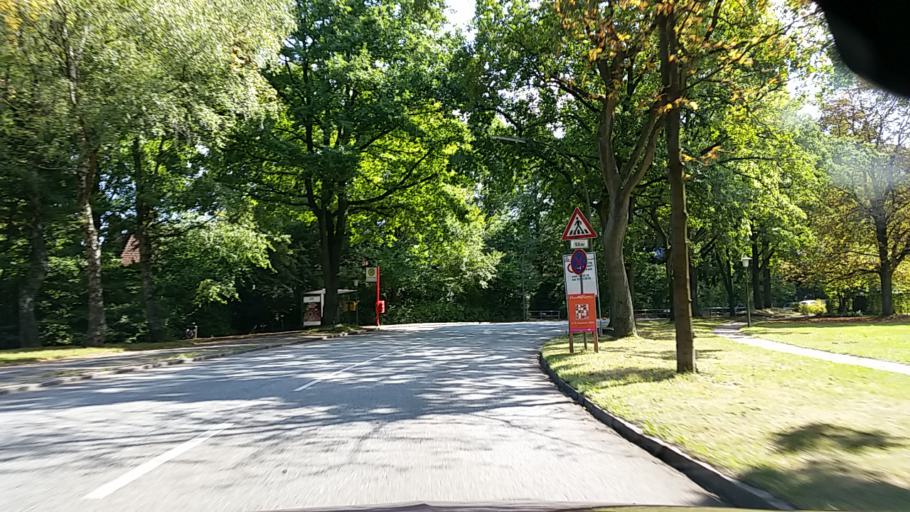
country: DE
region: Hamburg
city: Bergstedt
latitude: 53.6686
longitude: 10.1468
